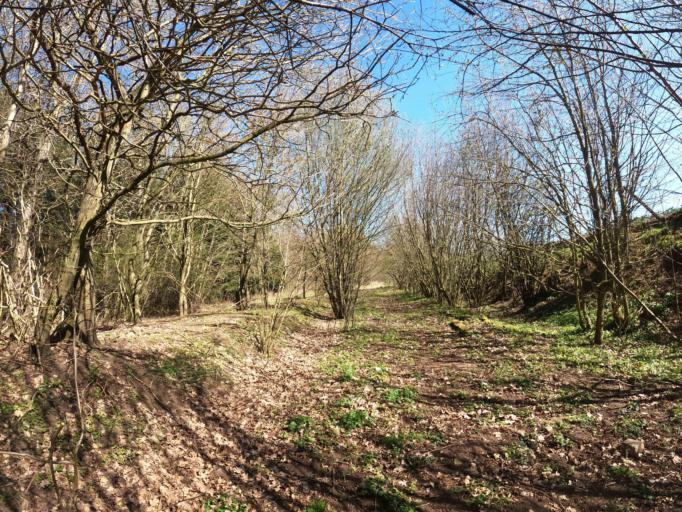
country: PL
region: West Pomeranian Voivodeship
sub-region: Powiat gryficki
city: Gryfice
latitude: 53.9291
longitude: 15.2645
